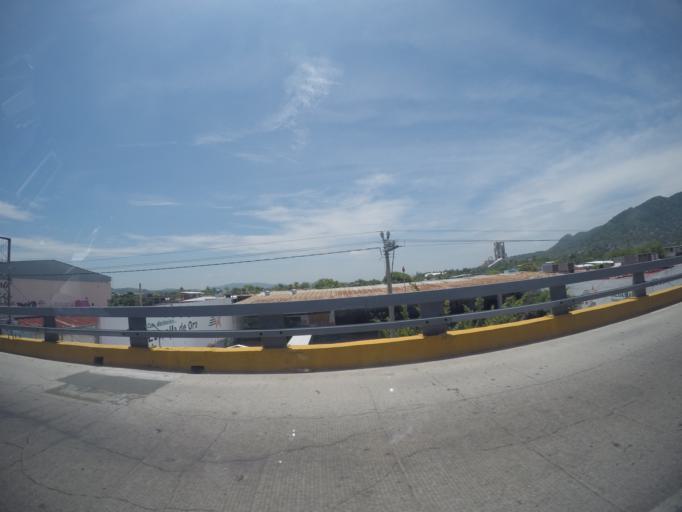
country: MX
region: Guerrero
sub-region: Acapulco de Juarez
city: Nueva Frontera
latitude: 16.8939
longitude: -99.8334
